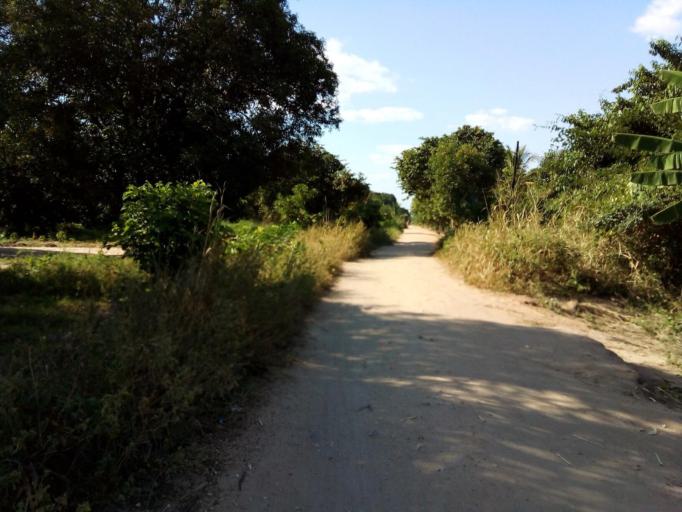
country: MZ
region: Zambezia
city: Quelimane
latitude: -17.6001
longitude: 36.8253
